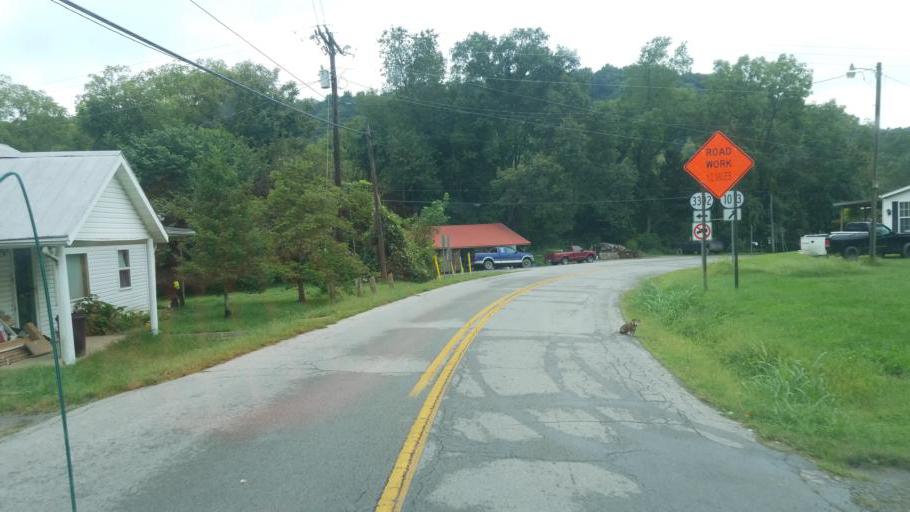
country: US
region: Kentucky
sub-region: Rowan County
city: Morehead
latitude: 38.3508
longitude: -83.5275
